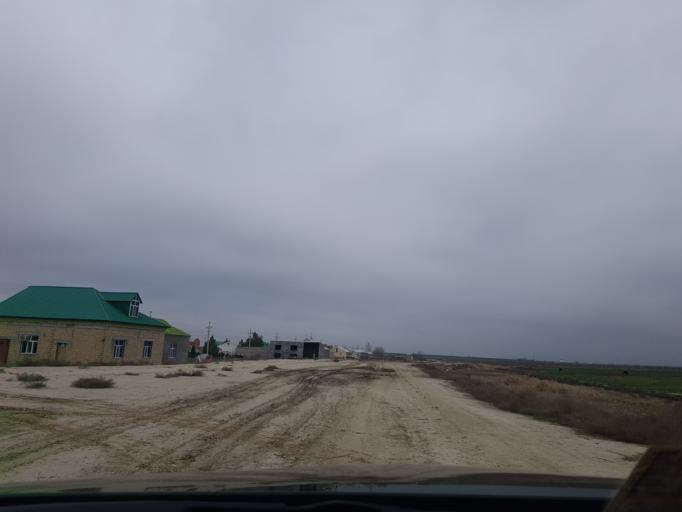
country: TM
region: Ahal
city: Abadan
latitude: 38.1431
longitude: 57.9652
